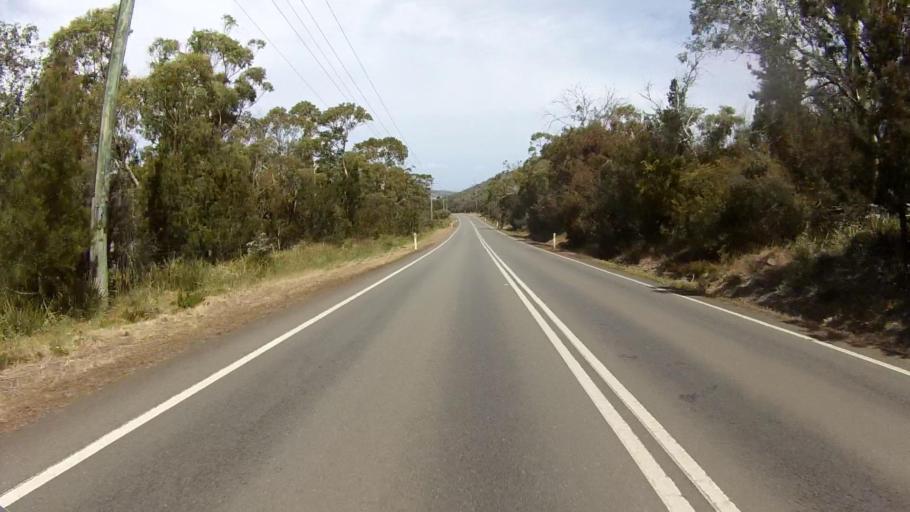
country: AU
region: Tasmania
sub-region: Clarence
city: Sandford
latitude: -43.0080
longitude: 147.4933
